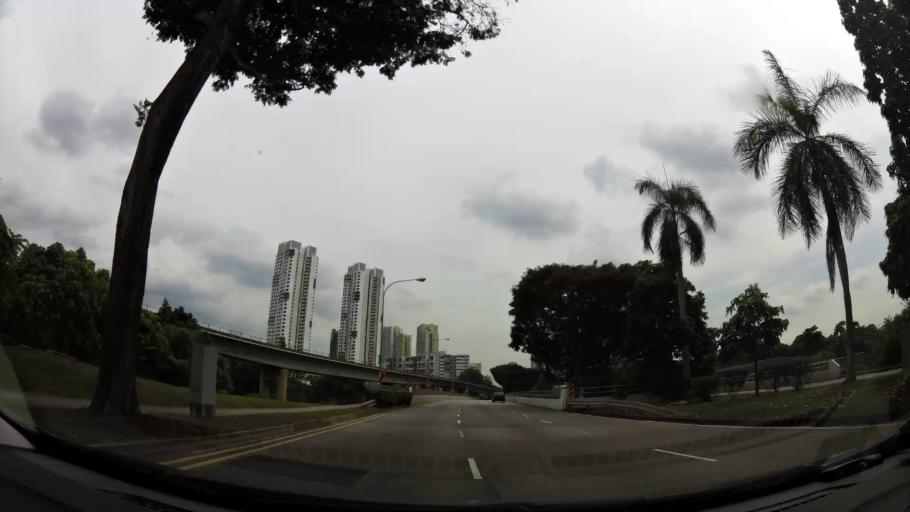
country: SG
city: Singapore
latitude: 1.3241
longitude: 103.7597
